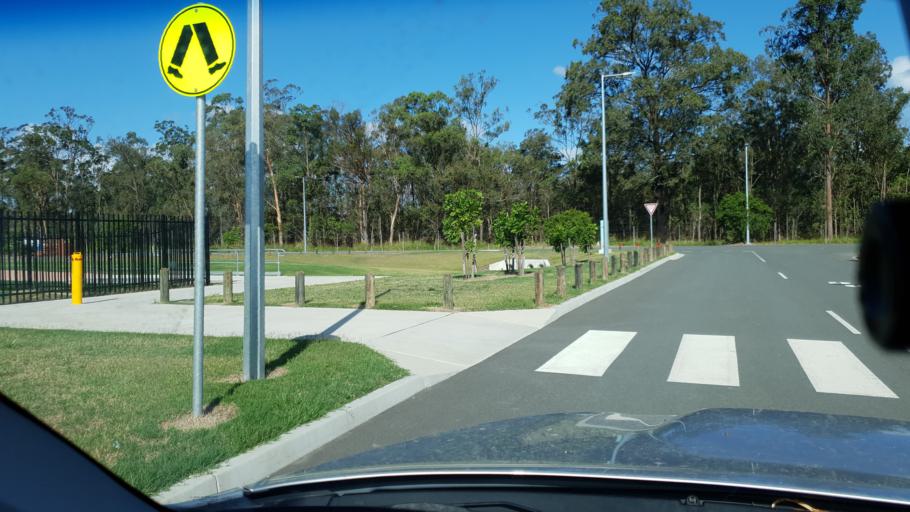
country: AU
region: Queensland
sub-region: Logan
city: Woodridge
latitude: -27.6715
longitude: 153.0699
